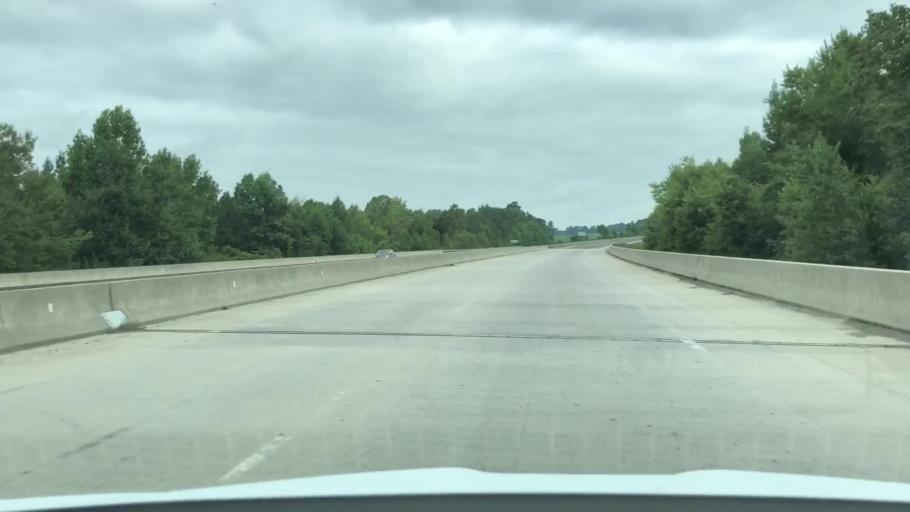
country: US
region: North Carolina
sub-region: Wayne County
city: Fremont
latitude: 35.5818
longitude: -77.9898
